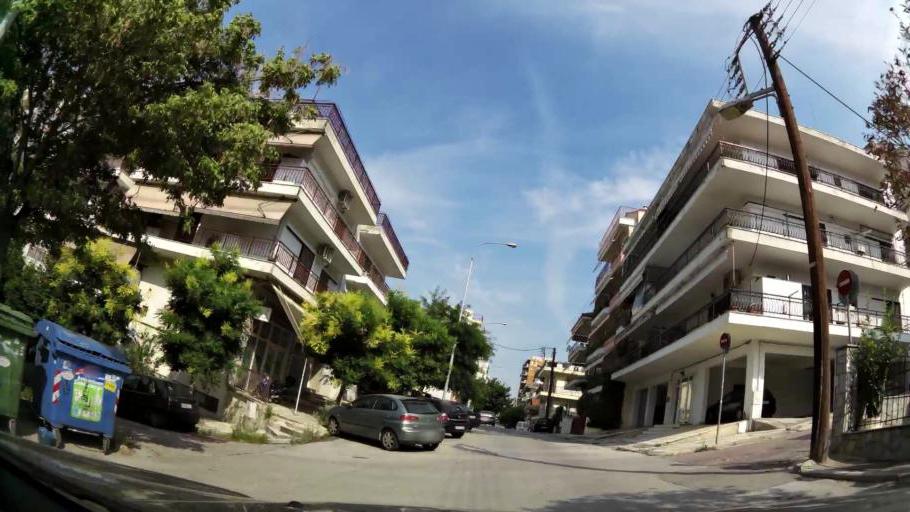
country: GR
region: Central Macedonia
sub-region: Nomos Thessalonikis
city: Sykies
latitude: 40.6524
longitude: 22.9543
